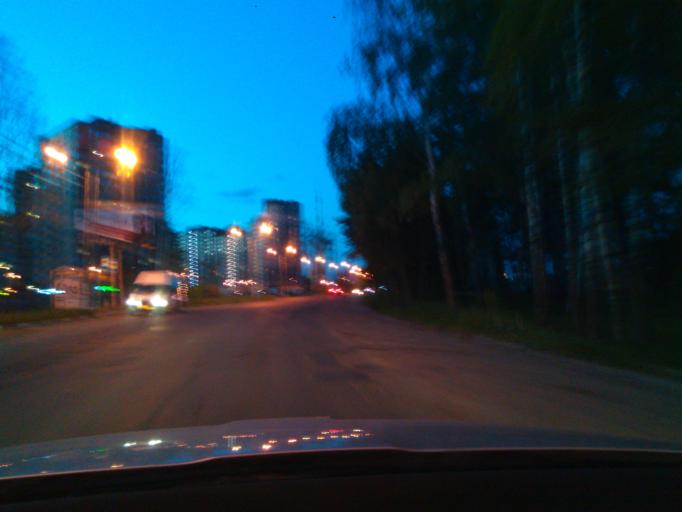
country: RU
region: Moskovskaya
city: Dolgoprudnyy
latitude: 55.9590
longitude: 37.5250
